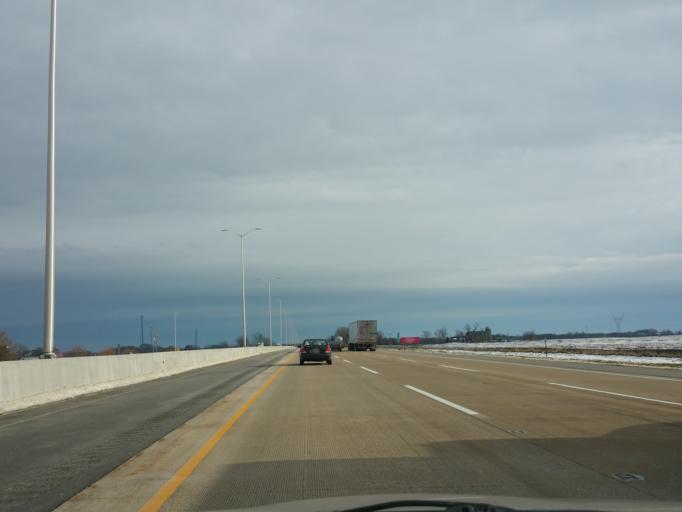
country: US
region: Illinois
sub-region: DeKalb County
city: Kingston
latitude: 42.2147
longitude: -88.7334
